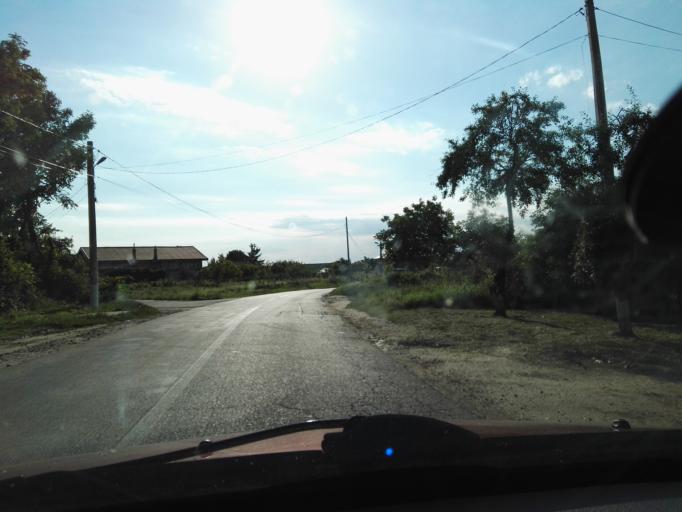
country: RO
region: Ilfov
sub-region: Comuna Copaceni
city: Copaceni
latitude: 44.2461
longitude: 26.0826
